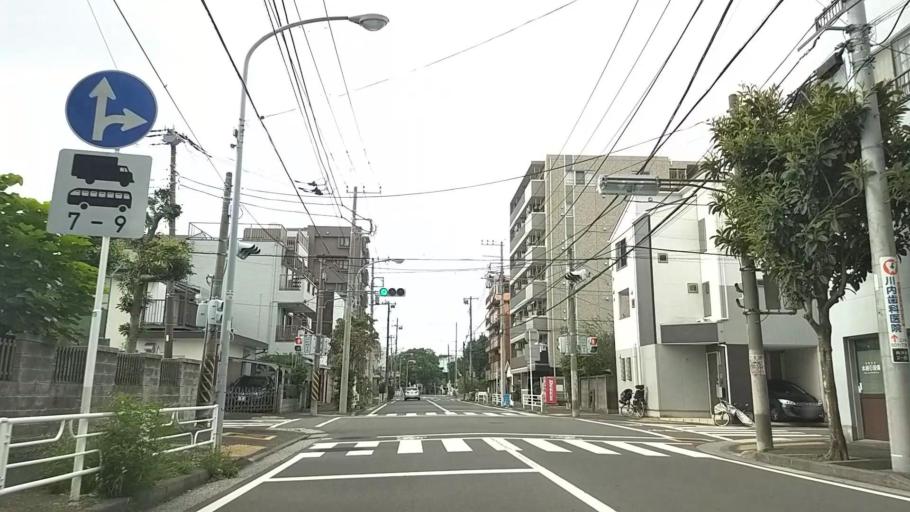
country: JP
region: Kanagawa
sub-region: Kawasaki-shi
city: Kawasaki
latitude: 35.5063
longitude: 139.6890
